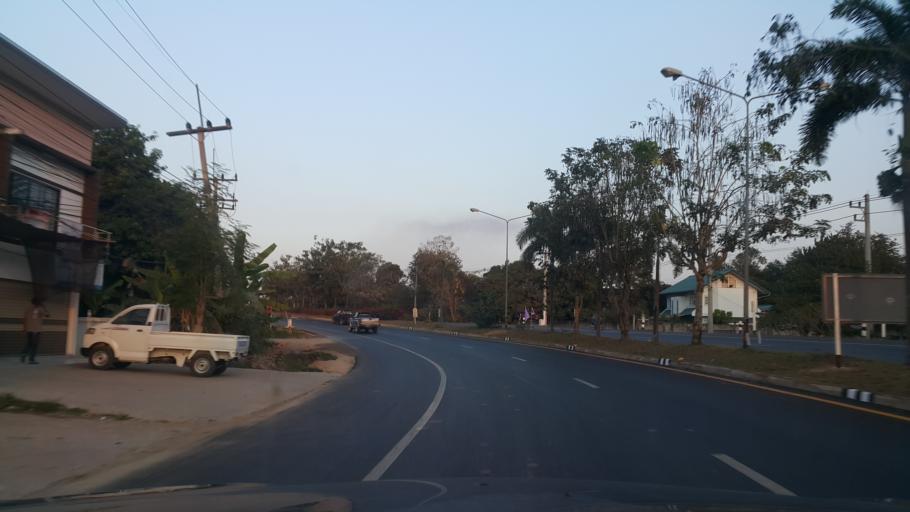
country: TH
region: Loei
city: Loei
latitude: 17.4908
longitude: 101.7032
